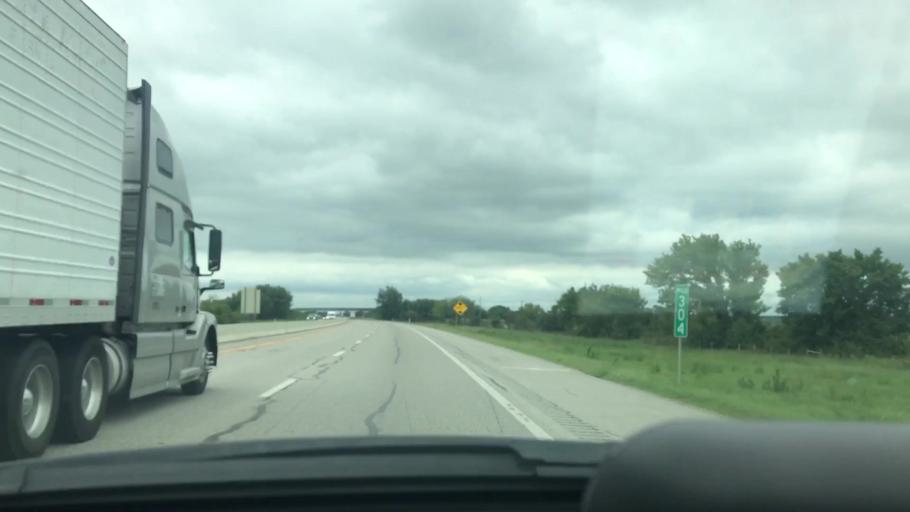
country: US
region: Oklahoma
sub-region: Ottawa County
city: Fairland
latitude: 36.7388
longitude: -94.9093
